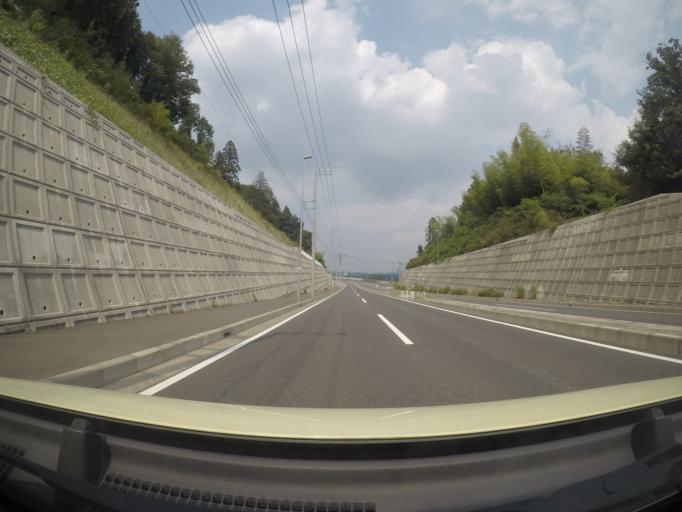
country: JP
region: Tokyo
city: Hachioji
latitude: 35.5779
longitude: 139.2851
